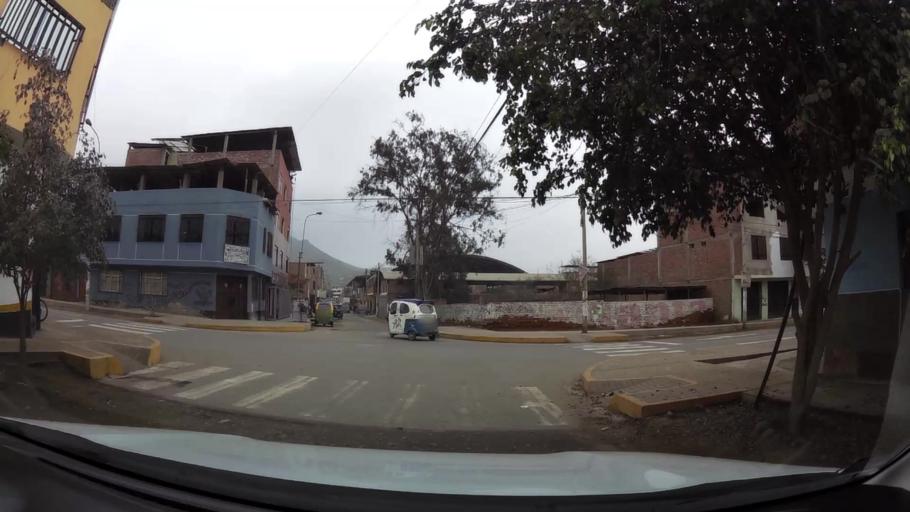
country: PE
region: Lima
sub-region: Lima
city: Surco
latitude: -12.2123
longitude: -76.9095
